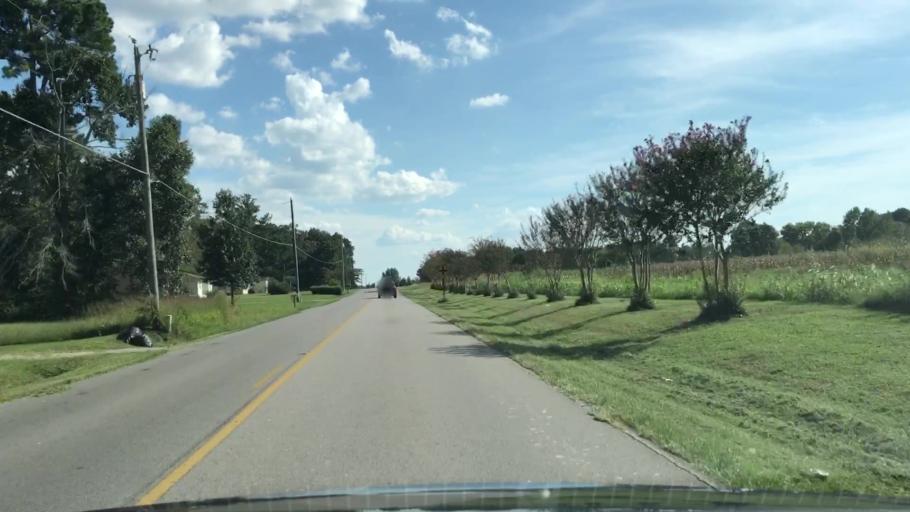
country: US
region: Alabama
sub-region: Madison County
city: Harvest
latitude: 34.8766
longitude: -86.7489
